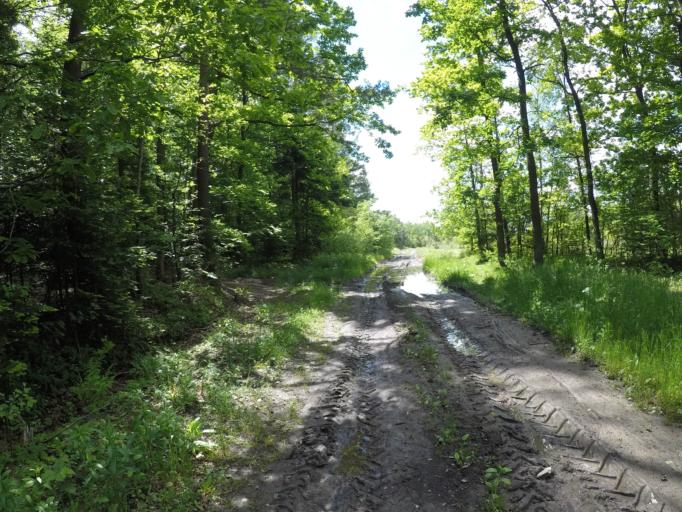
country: PL
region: Swietokrzyskie
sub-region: Powiat kielecki
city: Kostomloty Pierwsze
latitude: 50.9338
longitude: 20.6044
